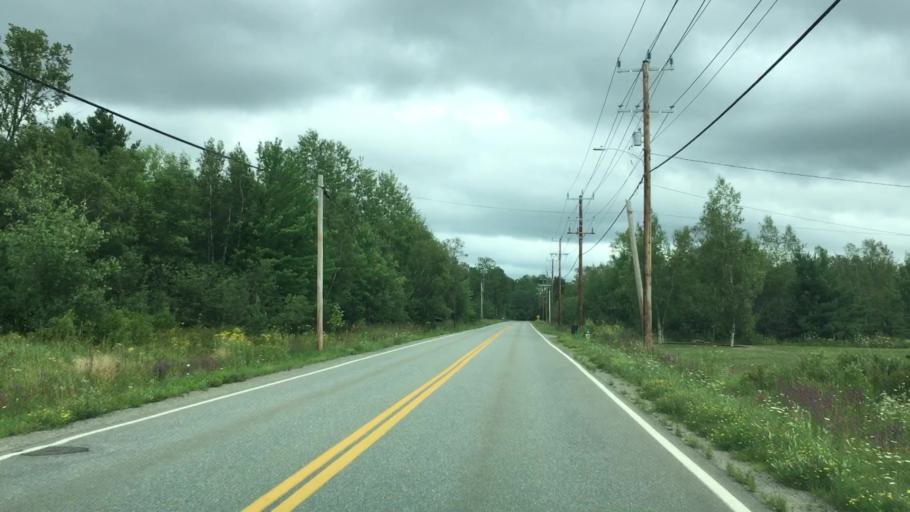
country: US
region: Maine
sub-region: Penobscot County
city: Brewer
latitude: 44.7675
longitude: -68.7614
